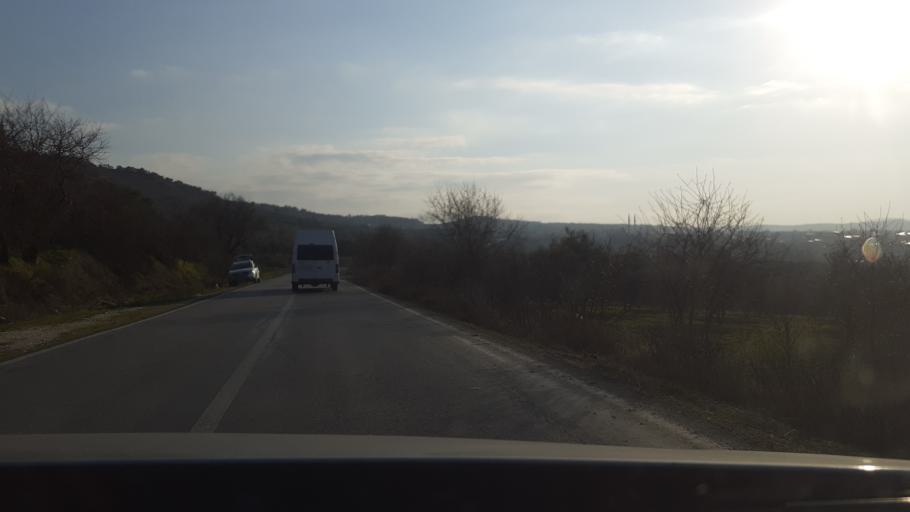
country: TR
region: Hatay
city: Oymakli
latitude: 36.1200
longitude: 36.3053
